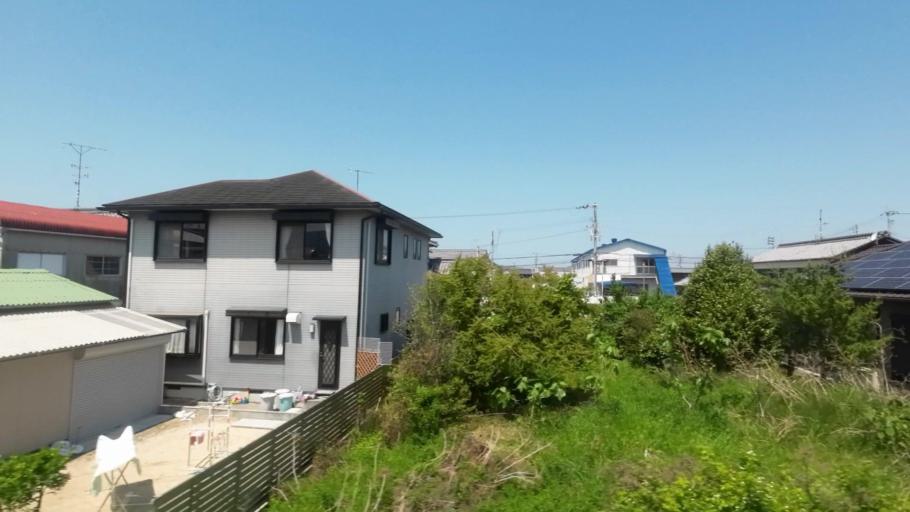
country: JP
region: Ehime
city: Hojo
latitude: 33.9780
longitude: 132.7778
